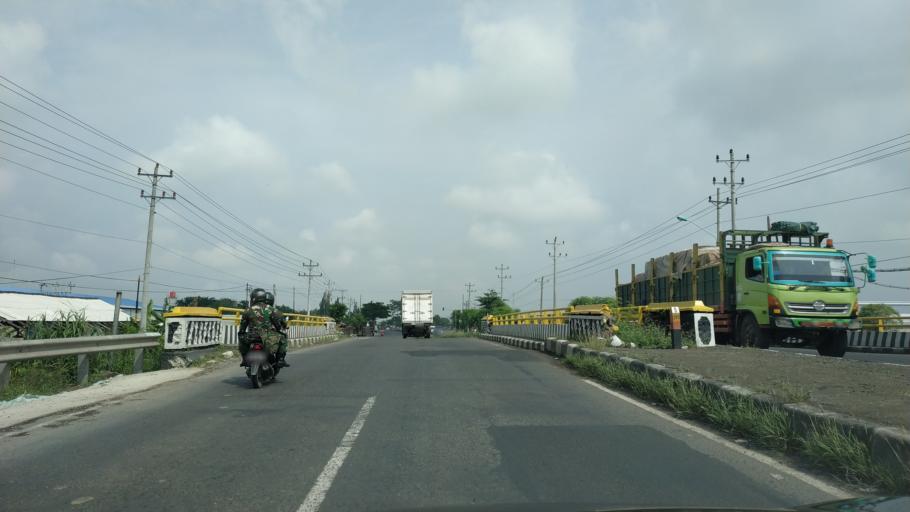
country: ID
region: Central Java
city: Bulakamba
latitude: -6.8724
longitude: 108.9091
